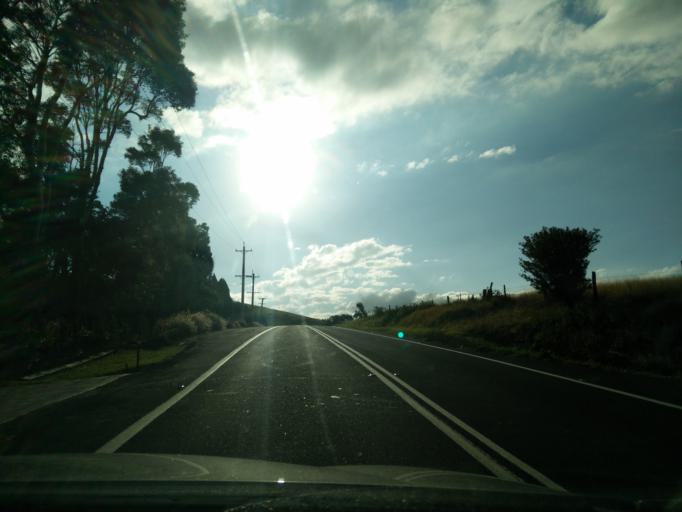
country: AU
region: New South Wales
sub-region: Shellharbour
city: Albion Park Rail
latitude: -34.6038
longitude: 150.7837
